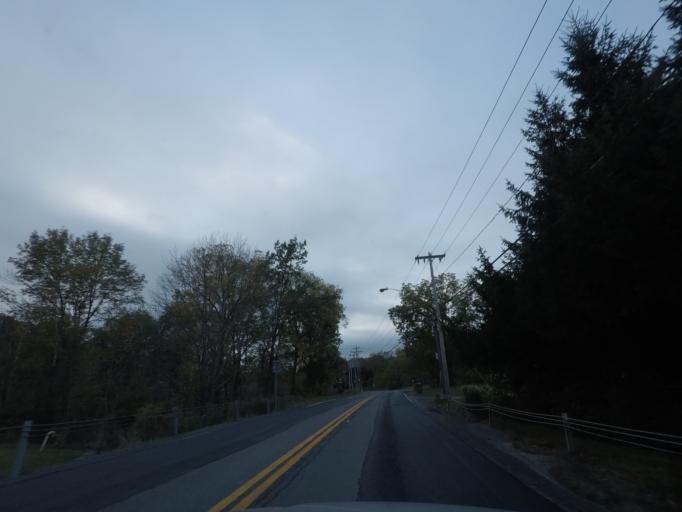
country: US
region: New York
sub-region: Rensselaer County
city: Nassau
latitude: 42.5623
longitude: -73.6367
